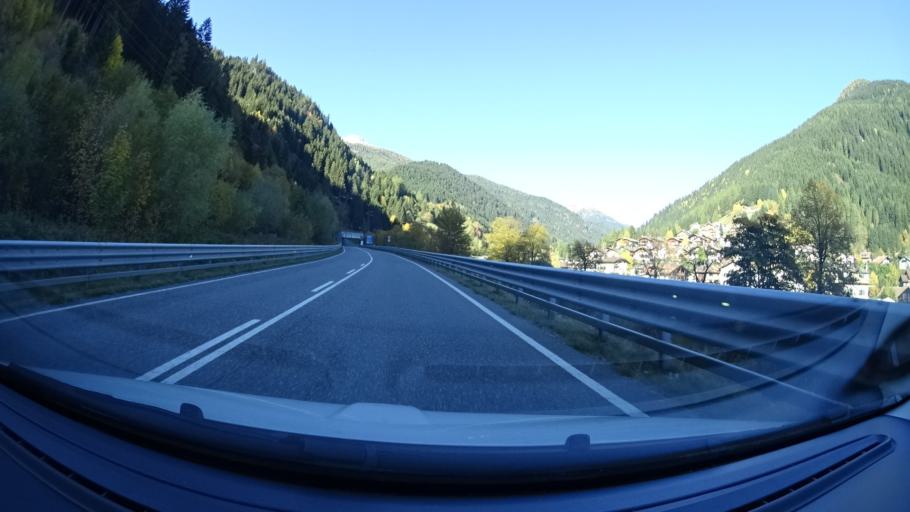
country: IT
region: Trentino-Alto Adige
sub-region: Provincia di Trento
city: Predazzo
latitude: 46.3163
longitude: 11.5955
